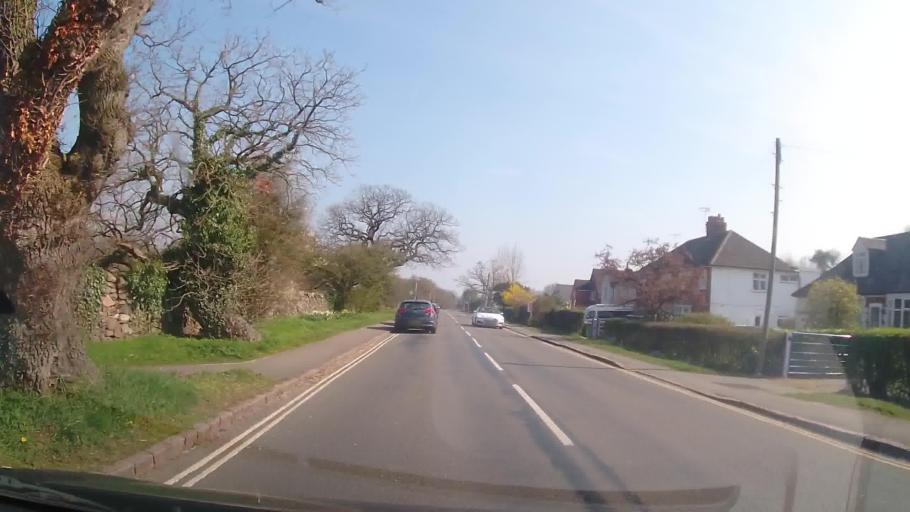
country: GB
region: England
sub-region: Leicestershire
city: Anstey
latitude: 52.6814
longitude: -1.2183
